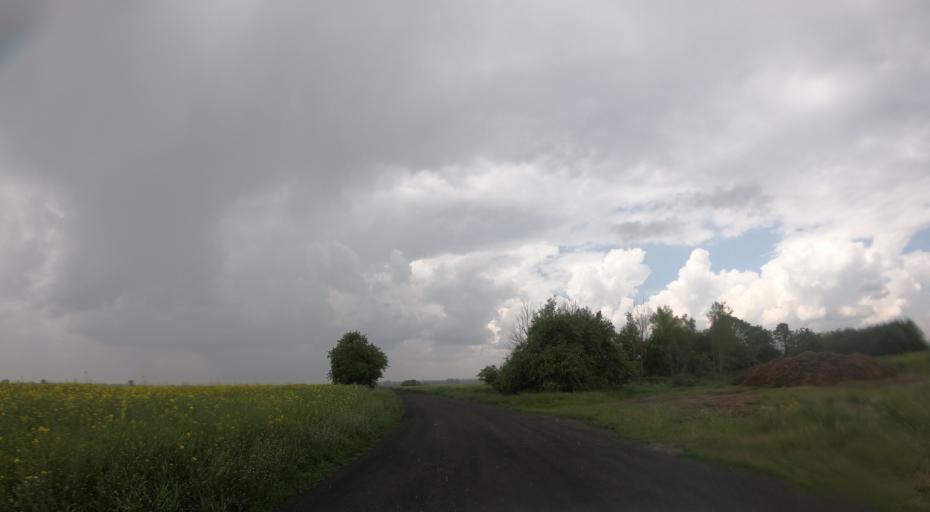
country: PL
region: West Pomeranian Voivodeship
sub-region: Powiat pyrzycki
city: Bielice
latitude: 53.2610
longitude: 14.7017
